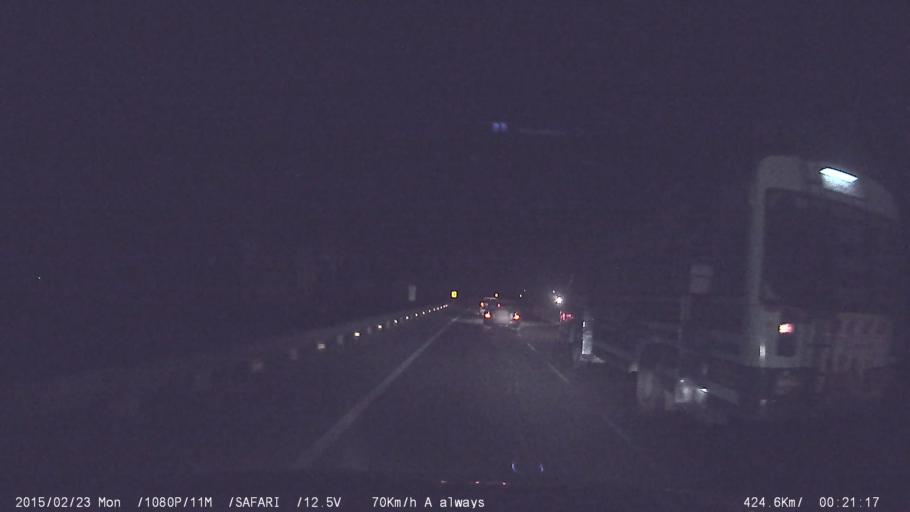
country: IN
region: Tamil Nadu
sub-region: Salem
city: Omalur
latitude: 11.8991
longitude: 78.0628
